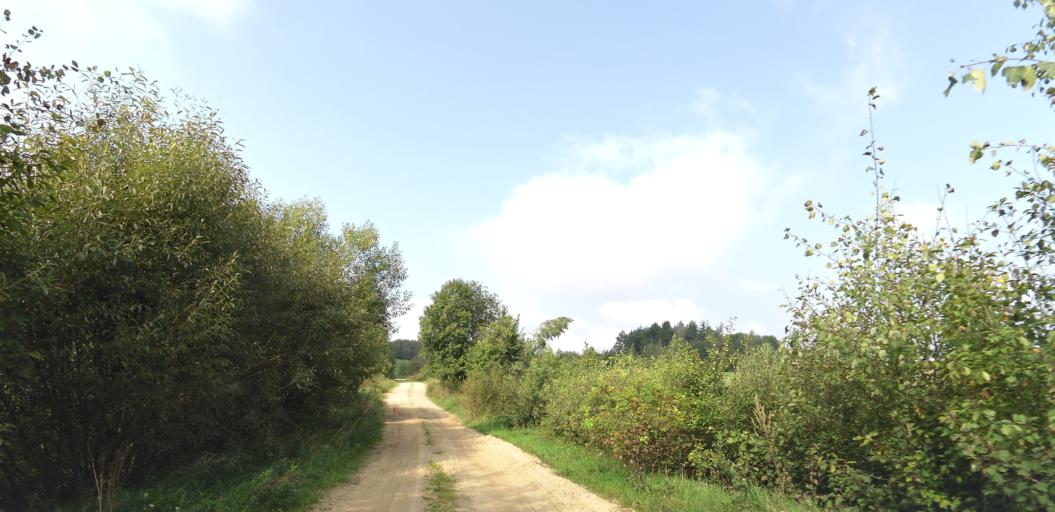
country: LT
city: Grigiskes
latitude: 54.7720
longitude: 25.0657
